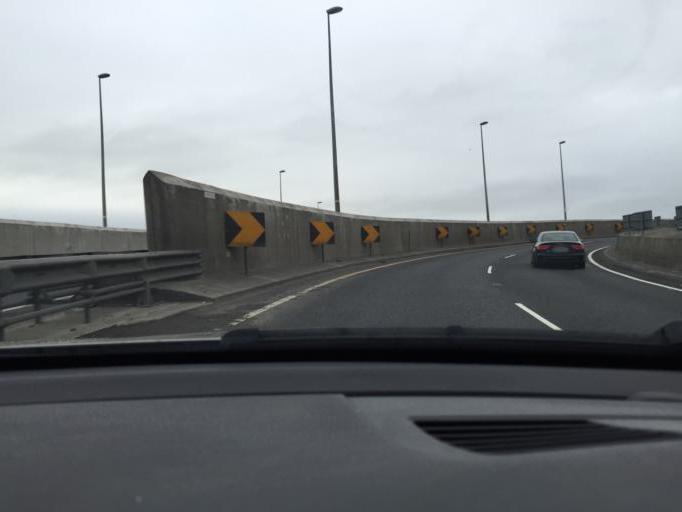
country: IE
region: Leinster
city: Castleknock
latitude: 53.3829
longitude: -6.3599
